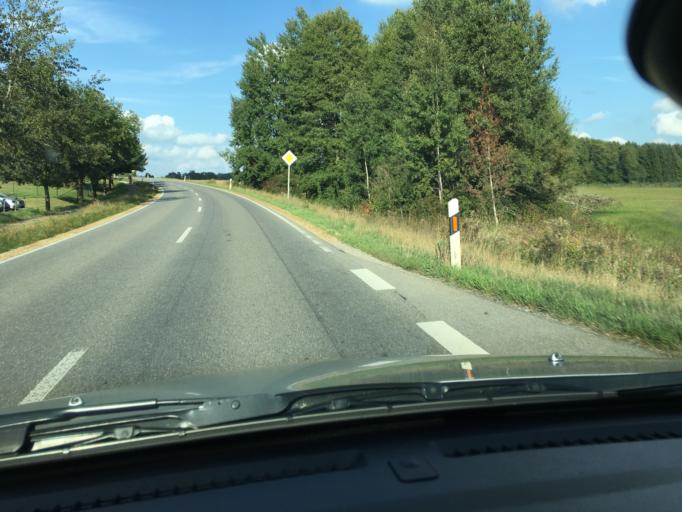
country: DE
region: Baden-Wuerttemberg
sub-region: Tuebingen Region
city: Bad Schussenried
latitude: 48.0012
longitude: 9.6684
